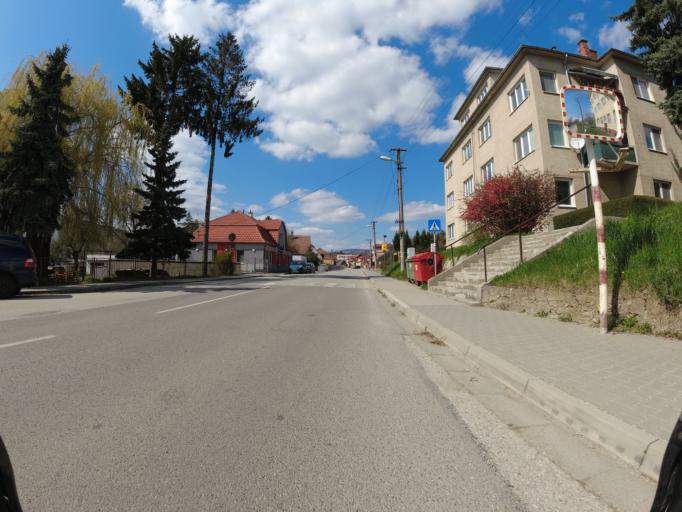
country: SK
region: Nitriansky
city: Stara Tura
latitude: 48.7751
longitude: 17.6985
